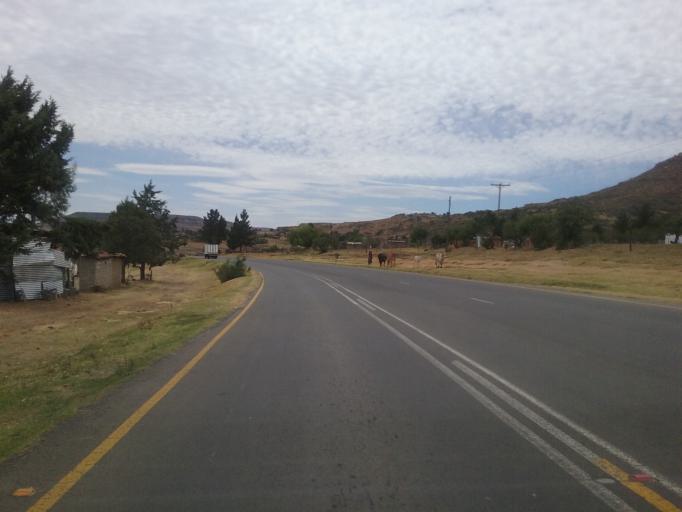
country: LS
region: Maseru
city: Nako
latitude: -29.6438
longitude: 27.4745
